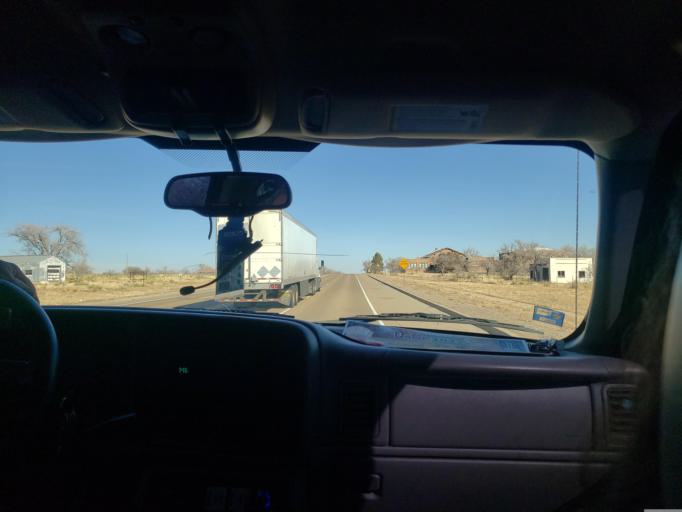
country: US
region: New Mexico
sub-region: Quay County
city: Logan
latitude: 35.6101
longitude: -103.0967
